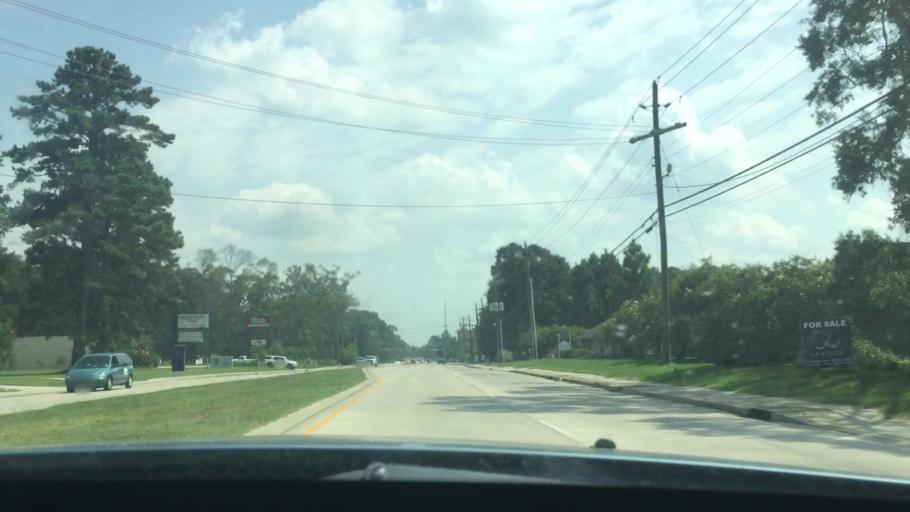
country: US
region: Louisiana
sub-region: East Baton Rouge Parish
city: Shenandoah
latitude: 30.4293
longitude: -91.0076
